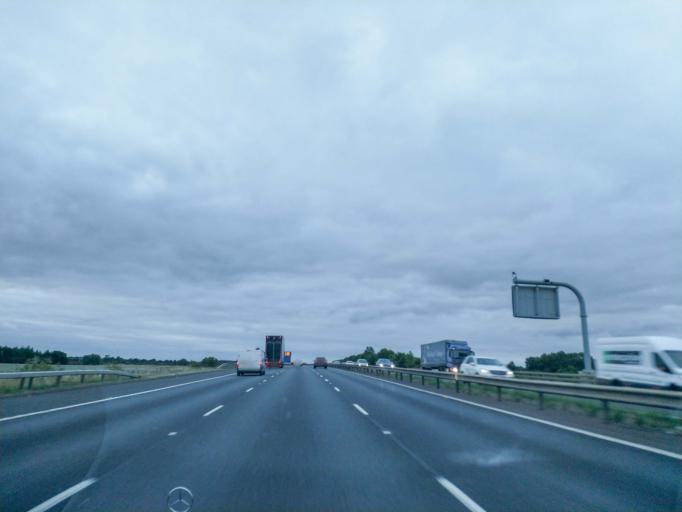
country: GB
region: England
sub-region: Oxfordshire
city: Bicester
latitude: 51.9264
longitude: -1.2022
